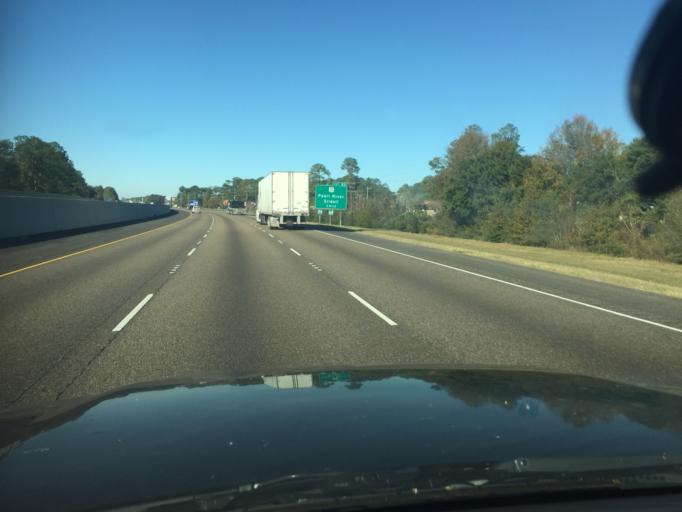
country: US
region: Louisiana
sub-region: Saint Tammany Parish
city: Slidell
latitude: 30.3098
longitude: -89.7539
